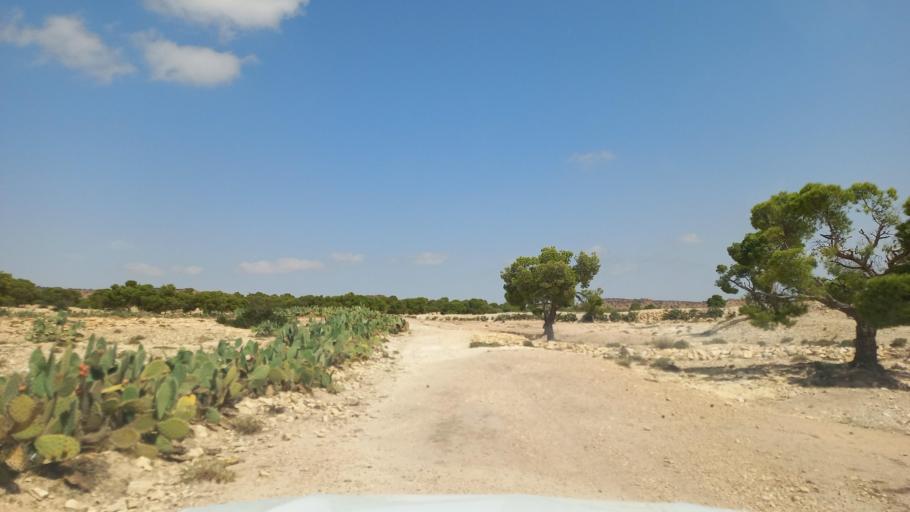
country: TN
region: Al Qasrayn
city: Sbiba
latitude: 35.4046
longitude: 8.9698
